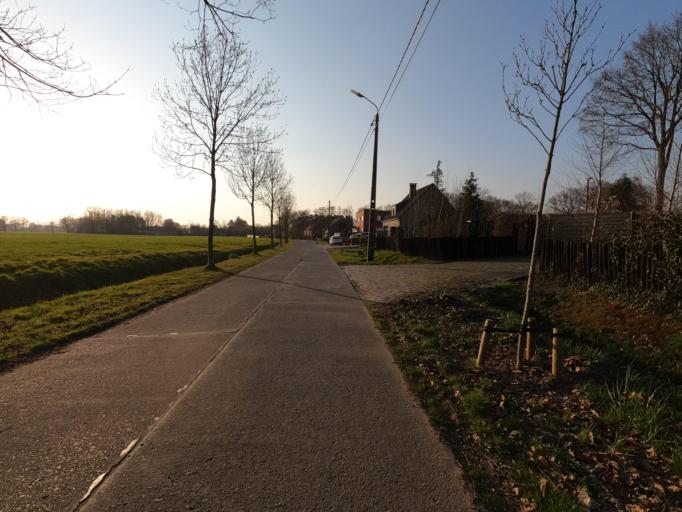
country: BE
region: Flanders
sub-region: Provincie Antwerpen
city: Hulshout
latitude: 51.0637
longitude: 4.7646
